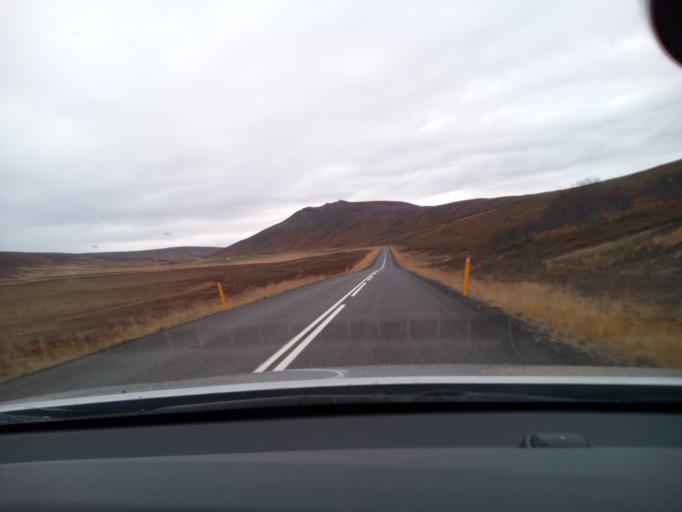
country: IS
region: Northeast
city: Laugar
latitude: 65.8131
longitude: -17.2697
